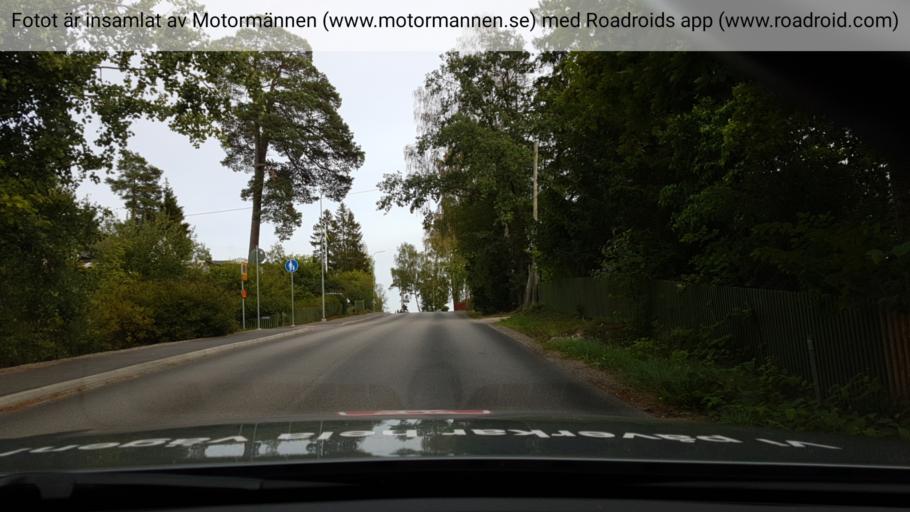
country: SE
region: Stockholm
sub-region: Haninge Kommun
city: Jordbro
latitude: 59.0825
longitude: 18.1536
